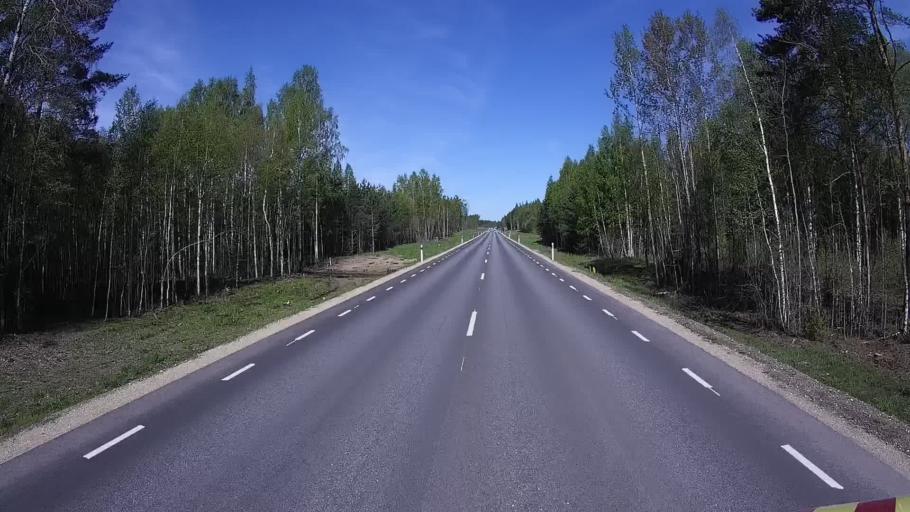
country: RU
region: Pskov
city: Pechory
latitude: 57.9681
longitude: 27.5950
